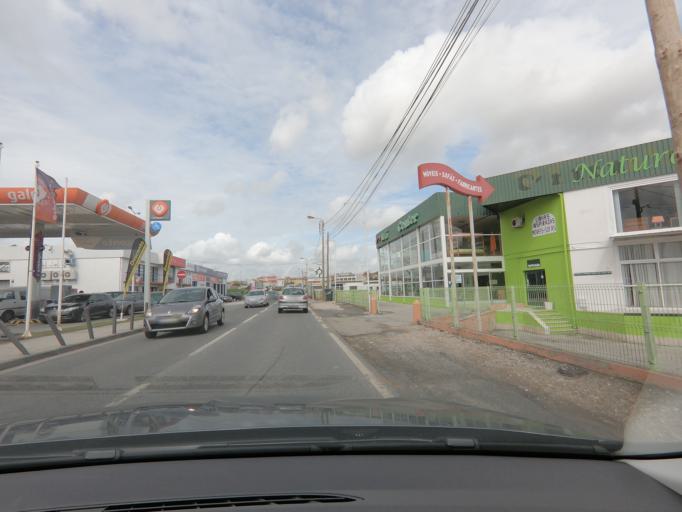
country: PT
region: Lisbon
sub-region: Cascais
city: Sao Domingos de Rana
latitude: 38.7224
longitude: -9.3373
